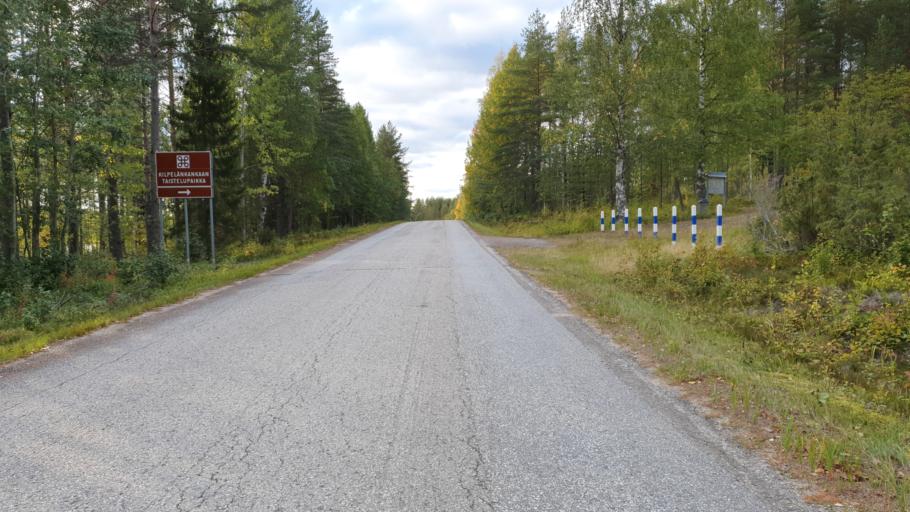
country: FI
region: North Karelia
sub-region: Pielisen Karjala
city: Lieksa
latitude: 63.9121
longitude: 30.1932
